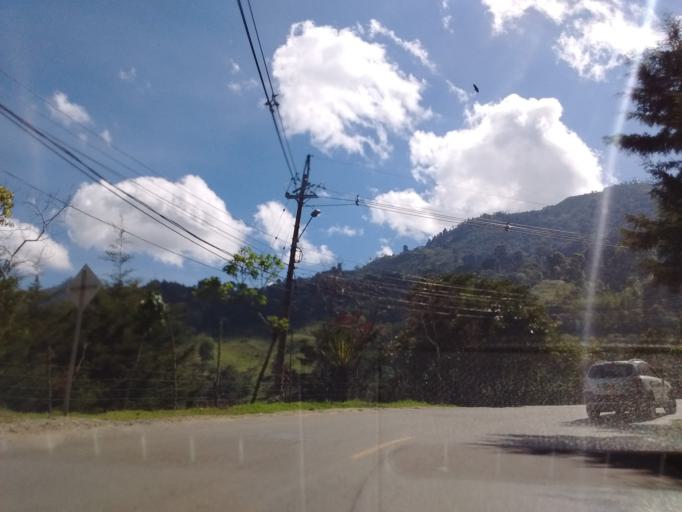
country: CO
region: Antioquia
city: Medellin
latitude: 6.2271
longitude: -75.5185
